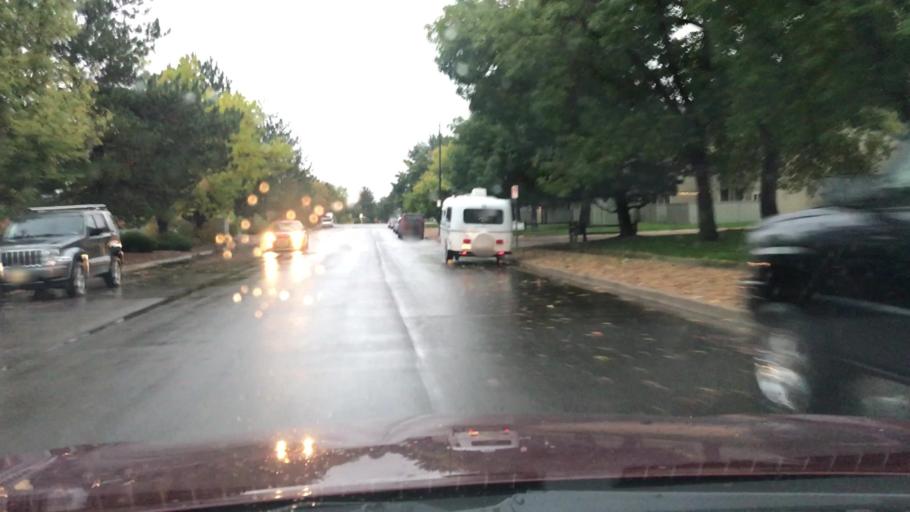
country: US
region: Colorado
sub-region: Boulder County
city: Gunbarrel
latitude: 40.0618
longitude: -105.2094
